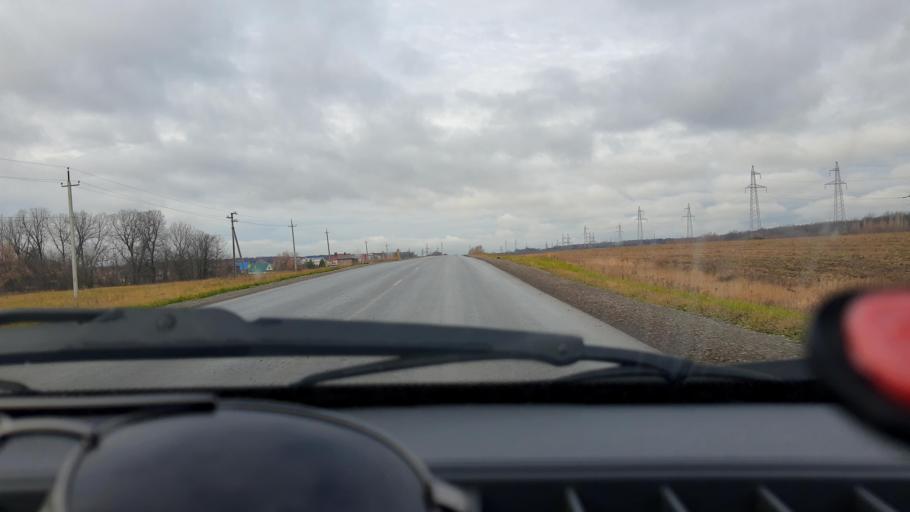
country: RU
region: Bashkortostan
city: Mikhaylovka
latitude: 54.8325
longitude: 55.9221
